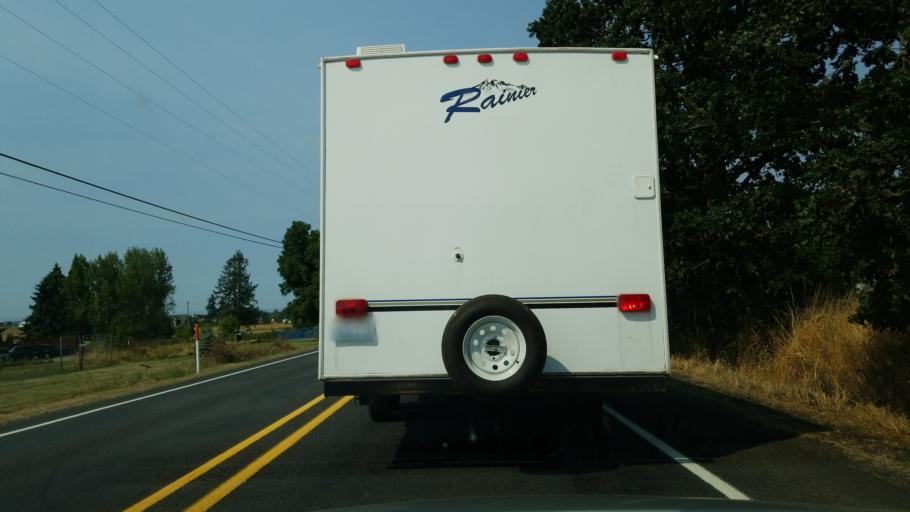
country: US
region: Oregon
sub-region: Marion County
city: Silverton
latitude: 44.9741
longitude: -122.8094
